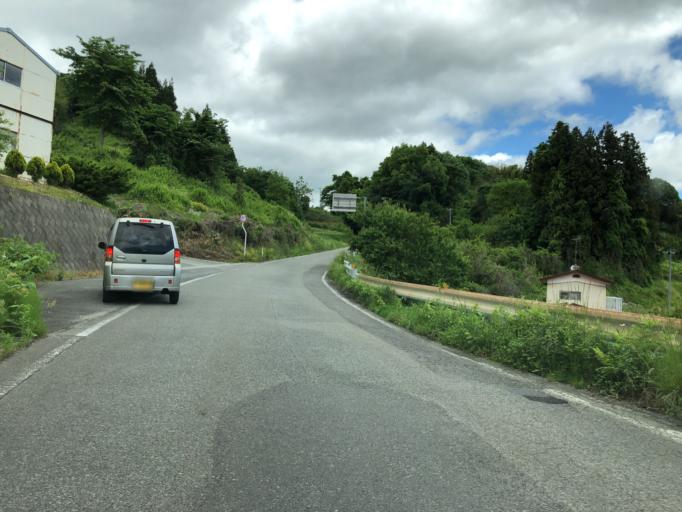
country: JP
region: Fukushima
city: Miharu
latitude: 37.4565
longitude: 140.4706
